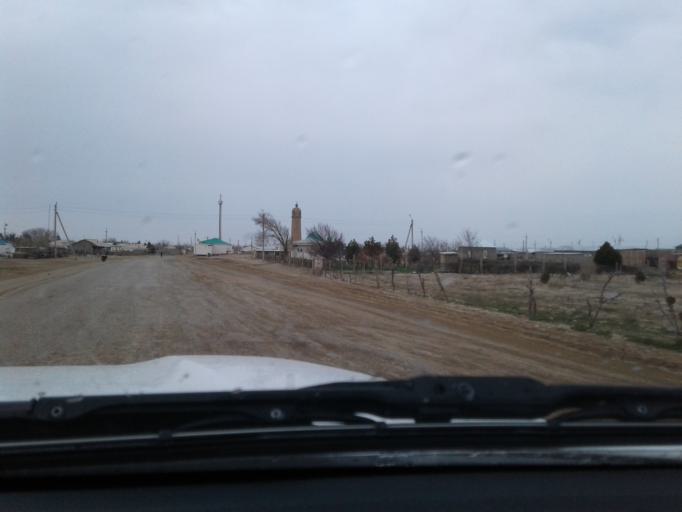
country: TM
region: Ahal
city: Abadan
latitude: 38.7596
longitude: 58.4918
